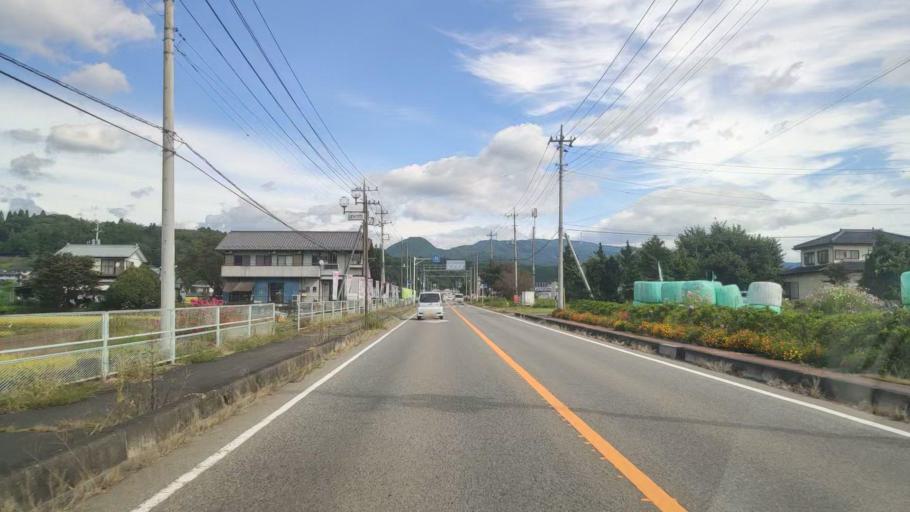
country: JP
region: Gunma
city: Nakanojomachi
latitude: 36.5951
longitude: 138.8623
